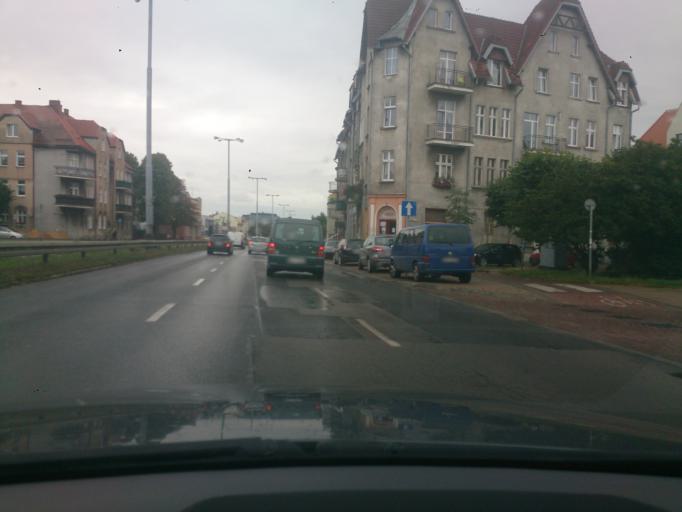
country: PL
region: Pomeranian Voivodeship
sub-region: Sopot
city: Sopot
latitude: 54.4094
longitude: 18.5680
